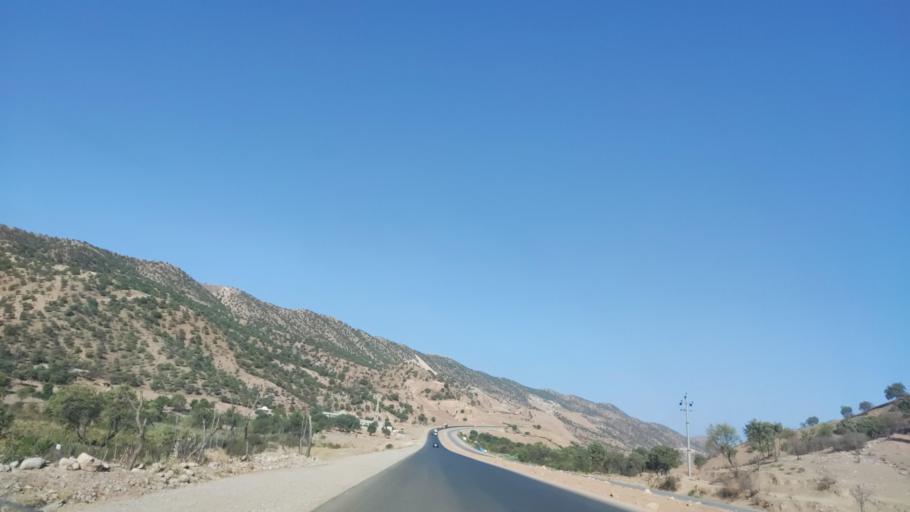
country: IQ
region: Arbil
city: Shaqlawah
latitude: 36.4305
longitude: 44.3217
